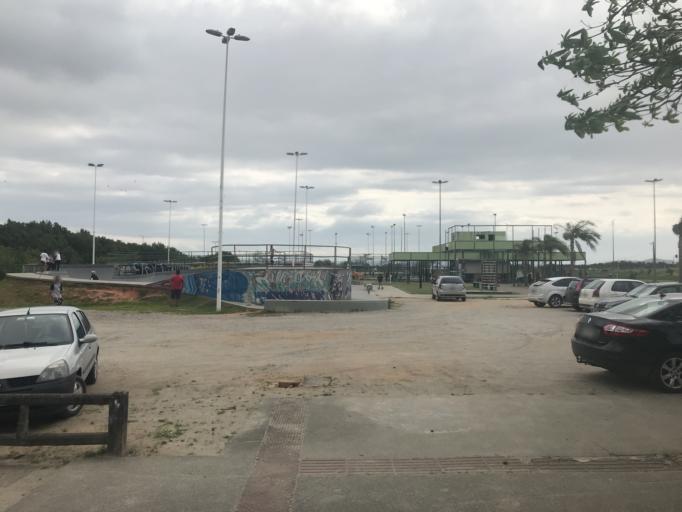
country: BR
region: Santa Catarina
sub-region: Florianopolis
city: Costeira do Pirajubae
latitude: -27.6296
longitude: -48.5242
